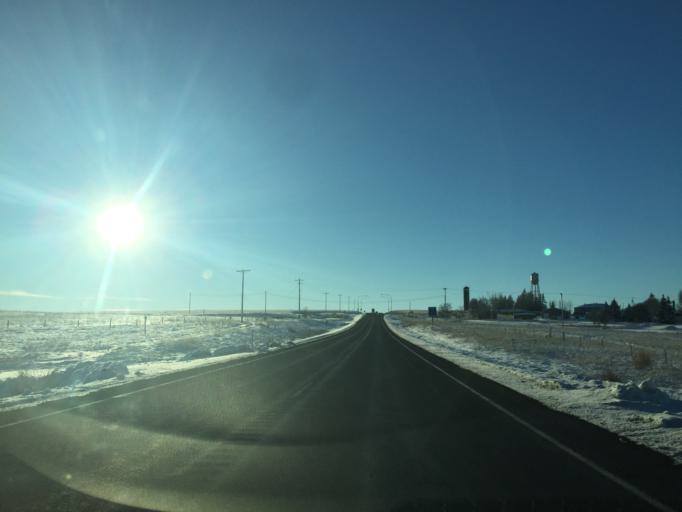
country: US
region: Washington
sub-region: Okanogan County
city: Coulee Dam
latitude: 47.7077
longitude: -118.9342
